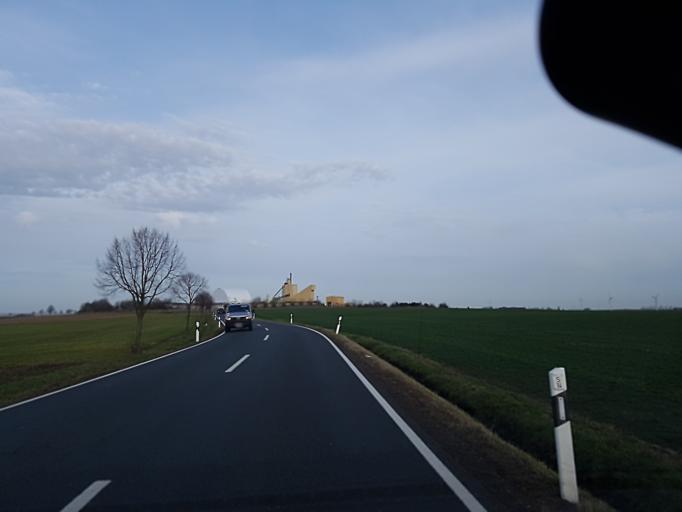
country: DE
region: Saxony
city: Bockelwitz
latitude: 51.1781
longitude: 12.9987
